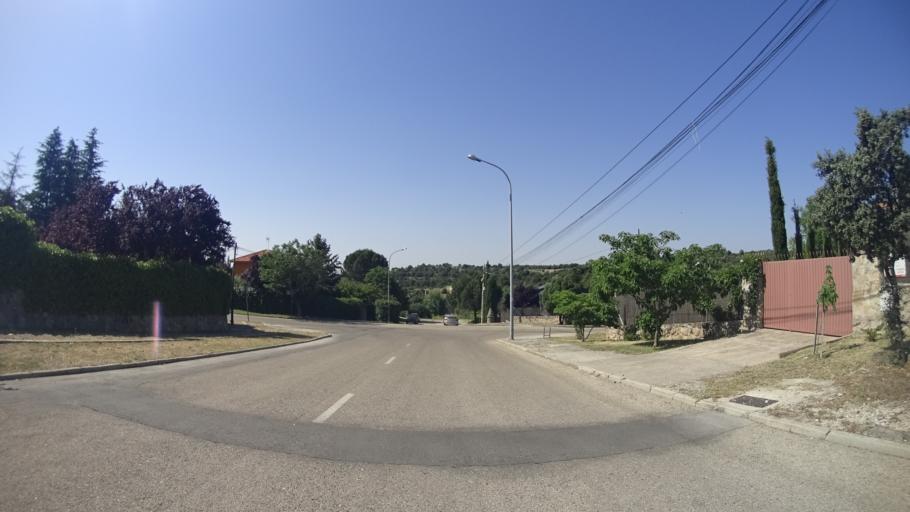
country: ES
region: Madrid
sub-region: Provincia de Madrid
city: Hoyo de Manzanares
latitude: 40.6039
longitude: -3.9043
